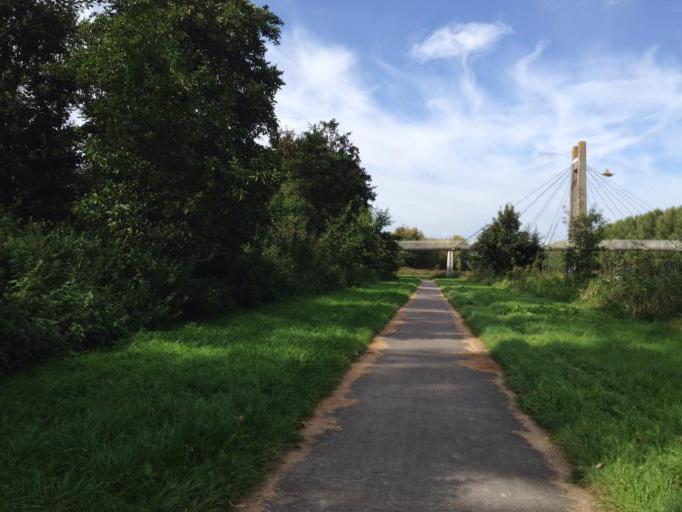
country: NL
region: Flevoland
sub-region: Gemeente Almere
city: Almere Stad
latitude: 52.3537
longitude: 5.2747
